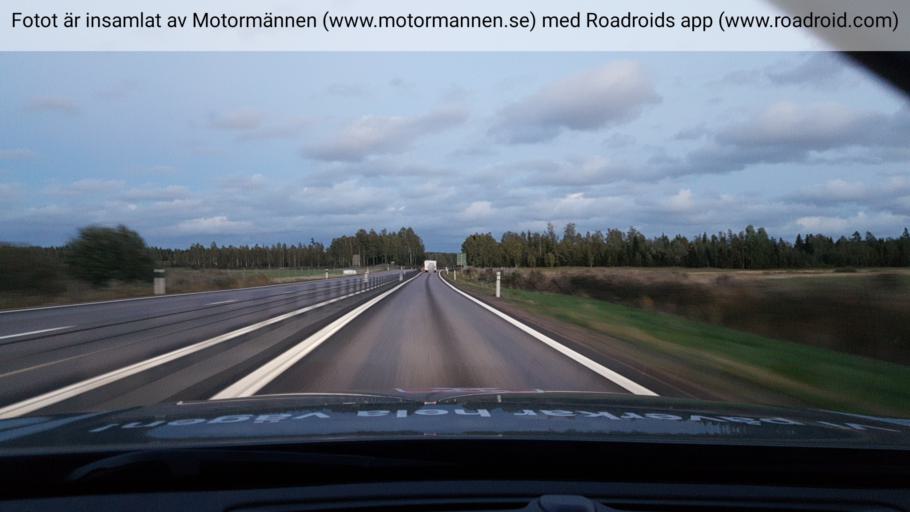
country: SE
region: Vaermland
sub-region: Karlstads Kommun
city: Skattkarr
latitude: 59.4148
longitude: 13.7452
